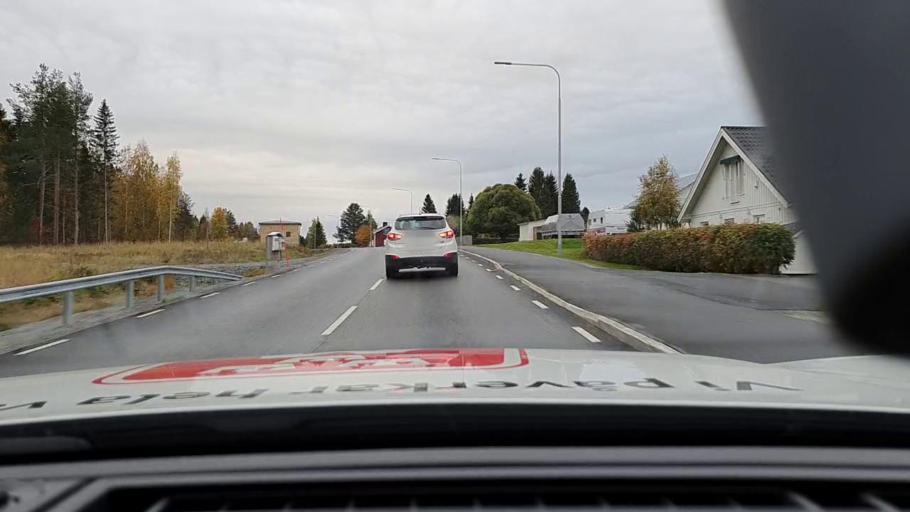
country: SE
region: Norrbotten
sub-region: Bodens Kommun
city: Saevast
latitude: 65.7754
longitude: 21.6946
